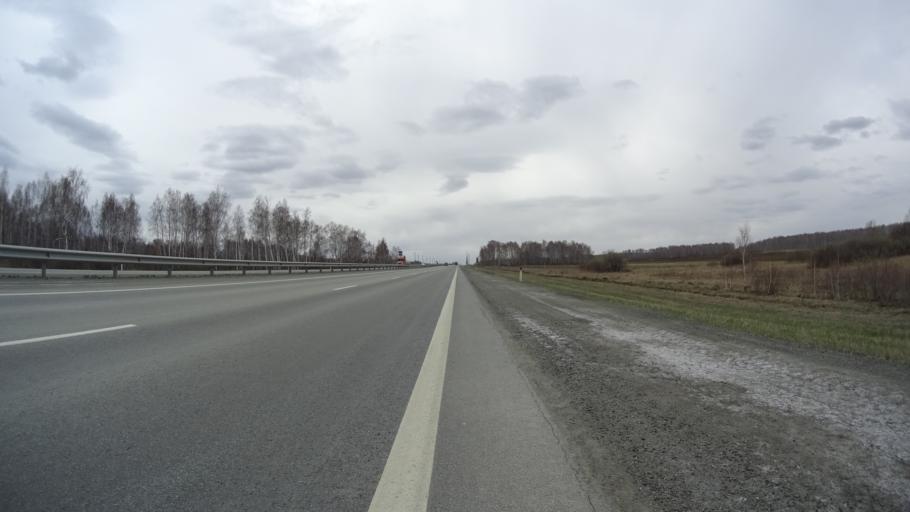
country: RU
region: Chelyabinsk
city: Yemanzhelinka
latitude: 54.8385
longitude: 61.3131
